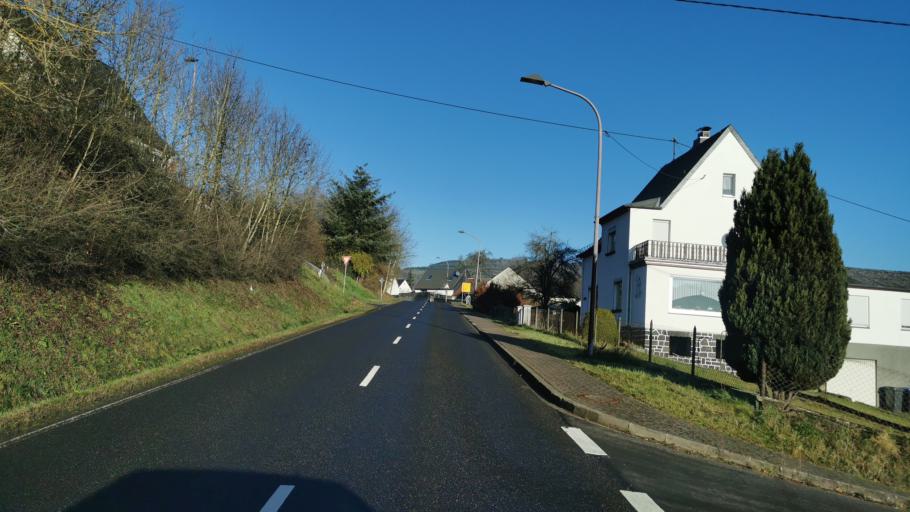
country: DE
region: Rheinland-Pfalz
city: Niederstadtfeld
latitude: 50.1746
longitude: 6.7665
